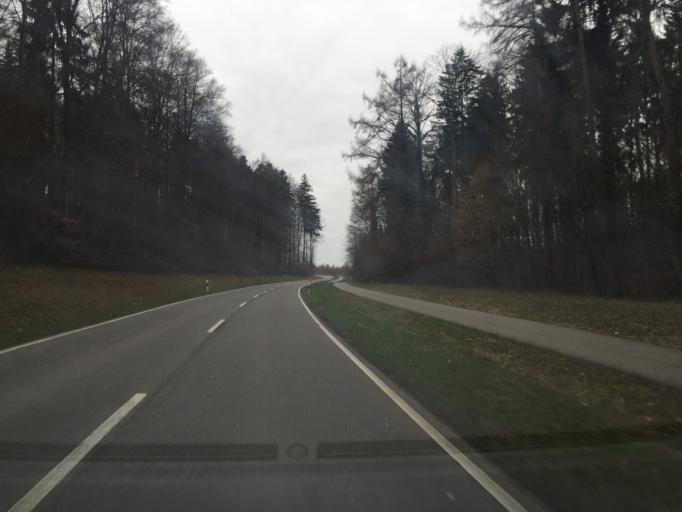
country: DE
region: Baden-Wuerttemberg
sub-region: Freiburg Region
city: Gailingen
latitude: 47.7093
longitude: 8.7441
